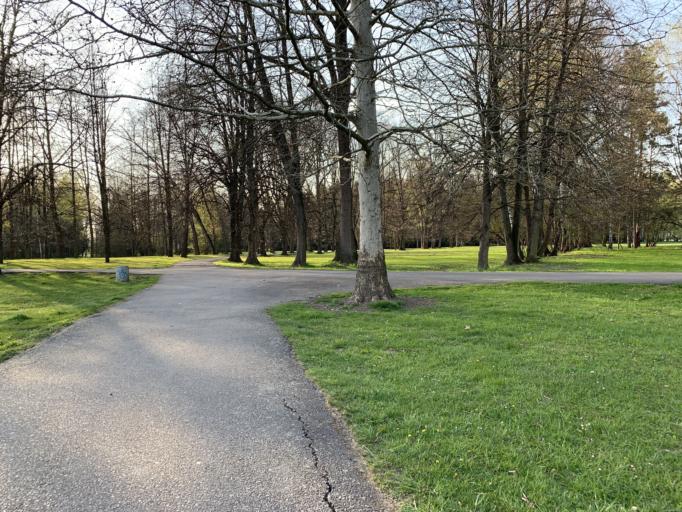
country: CZ
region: Jihocesky
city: Litvinovice
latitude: 48.9691
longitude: 14.4611
